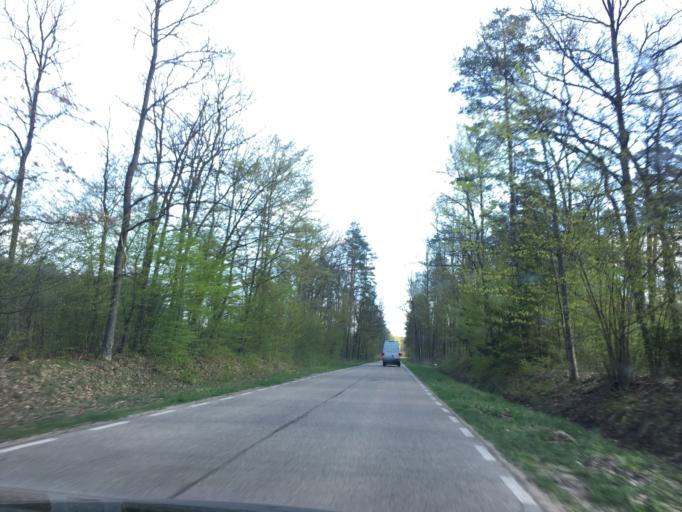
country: PL
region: Warmian-Masurian Voivodeship
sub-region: Powiat piski
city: Ruciane-Nida
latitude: 53.6691
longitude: 21.5741
